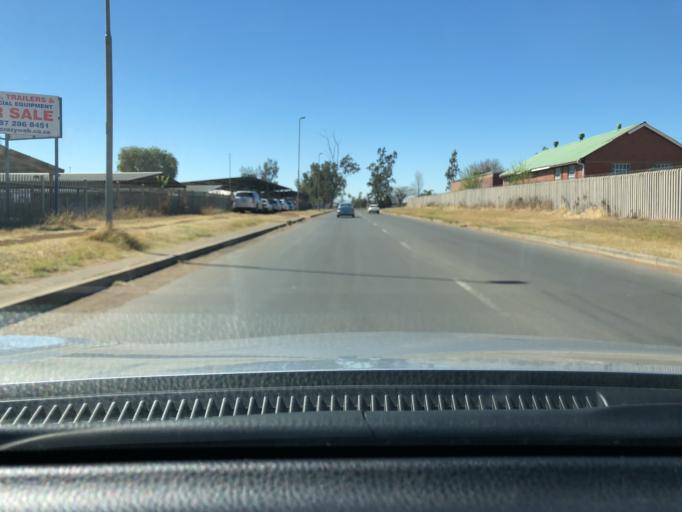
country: ZA
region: KwaZulu-Natal
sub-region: Amajuba District Municipality
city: Newcastle
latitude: -27.7602
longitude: 29.9504
